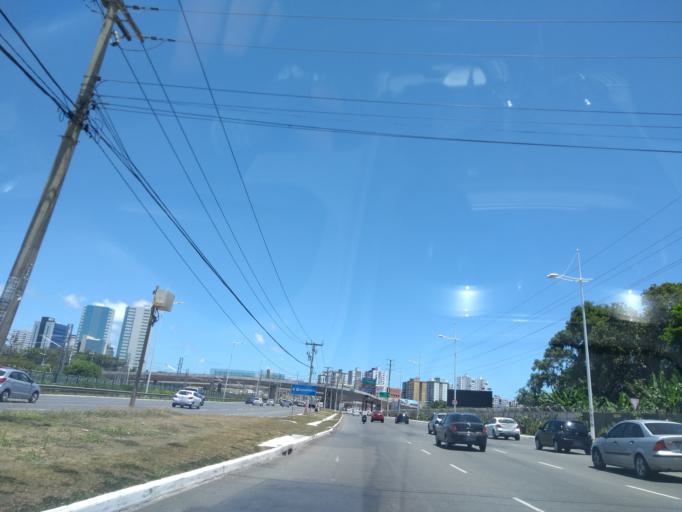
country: BR
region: Bahia
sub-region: Salvador
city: Salvador
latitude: -12.9705
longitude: -38.4426
